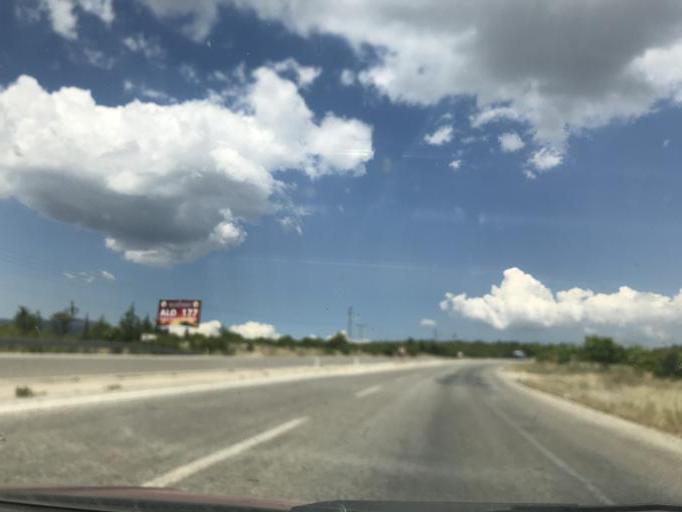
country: TR
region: Denizli
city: Tavas
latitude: 37.5915
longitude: 29.1084
